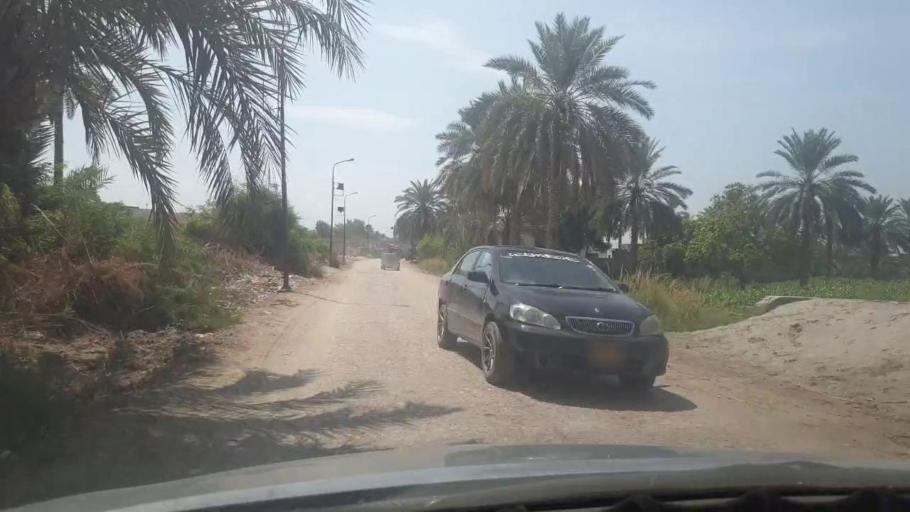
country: PK
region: Sindh
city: Bozdar
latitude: 27.1955
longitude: 68.5873
